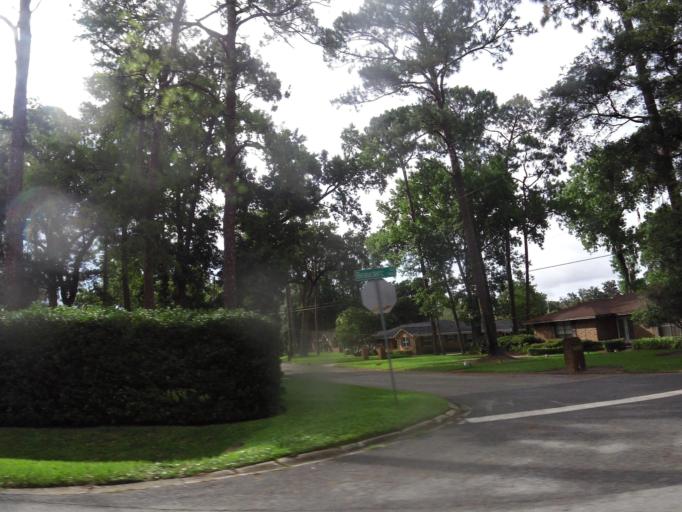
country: US
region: Florida
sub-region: Clay County
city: Orange Park
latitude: 30.2088
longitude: -81.6258
